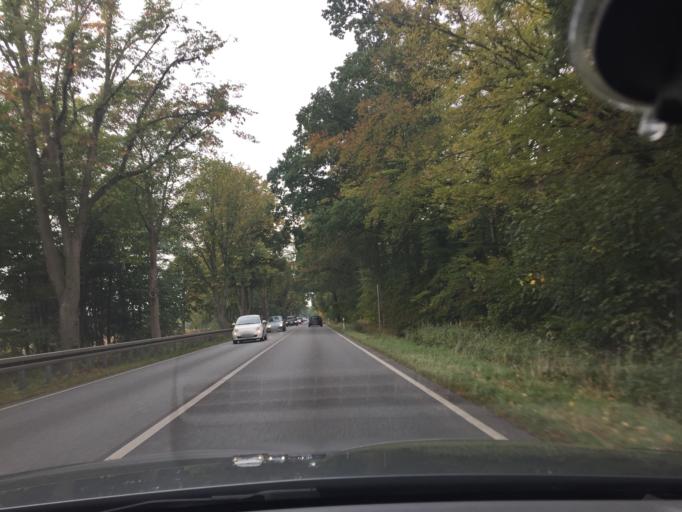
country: DE
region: Mecklenburg-Vorpommern
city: Bartenshagen-Parkentin
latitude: 54.1080
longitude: 11.9576
